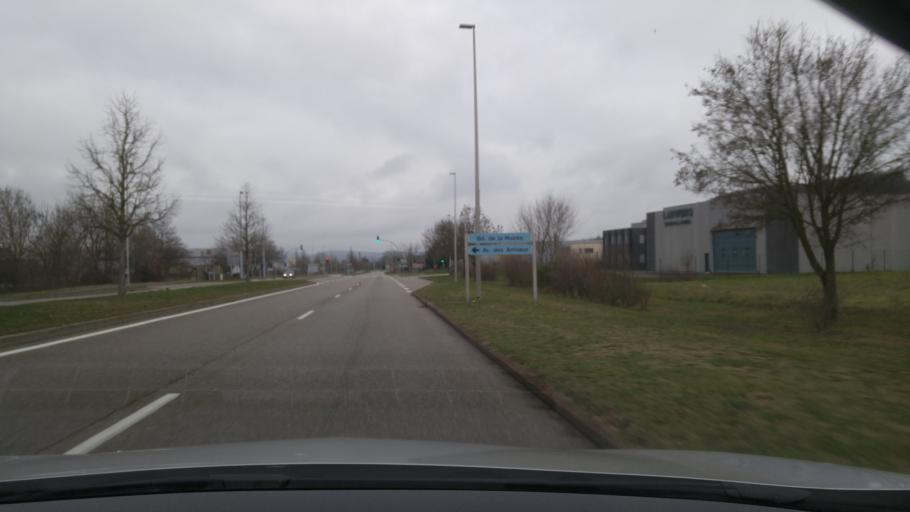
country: FR
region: Rhone-Alpes
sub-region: Departement de l'Isere
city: Saint-Quentin-Fallavier
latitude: 45.6396
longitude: 5.1133
